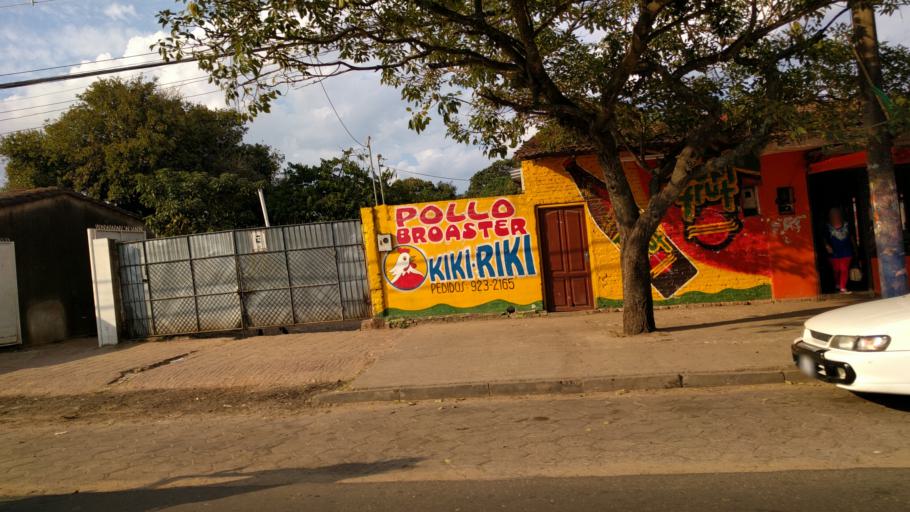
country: BO
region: Santa Cruz
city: Warnes
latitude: -17.5125
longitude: -63.1667
